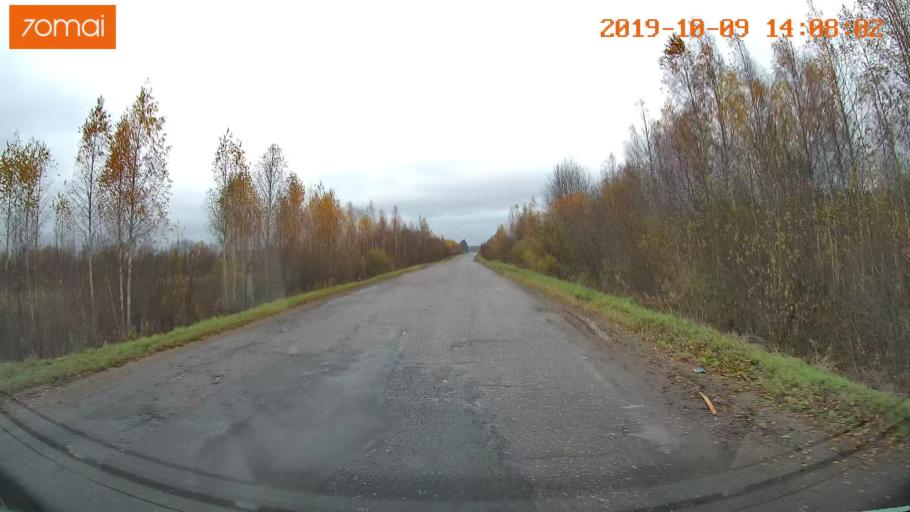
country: RU
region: Kostroma
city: Buy
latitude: 58.4744
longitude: 41.4307
